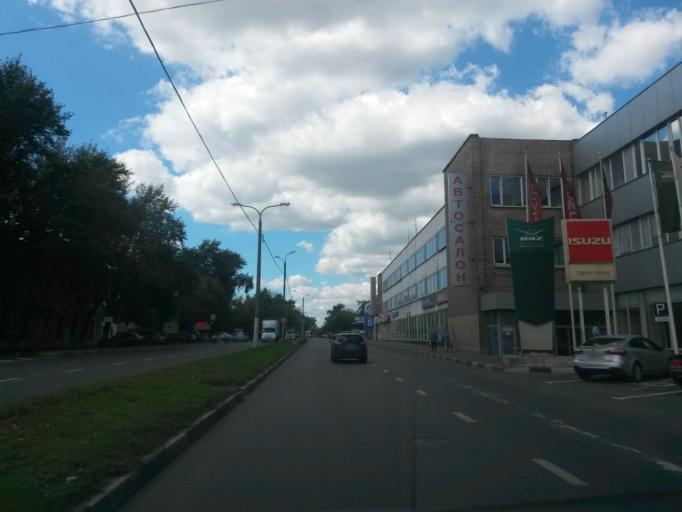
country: RU
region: Moscow
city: Mar'ino
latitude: 55.6575
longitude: 37.7252
